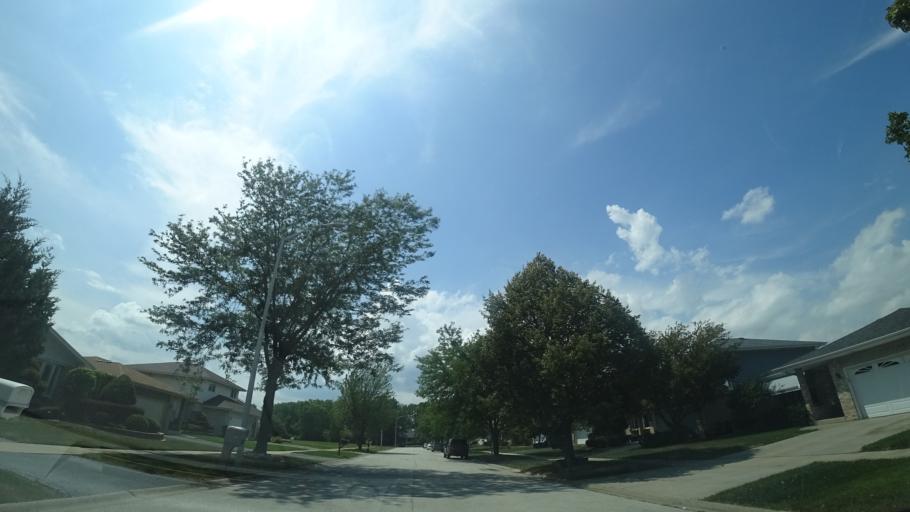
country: US
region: Illinois
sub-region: Cook County
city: Crestwood
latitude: 41.6715
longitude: -87.7500
